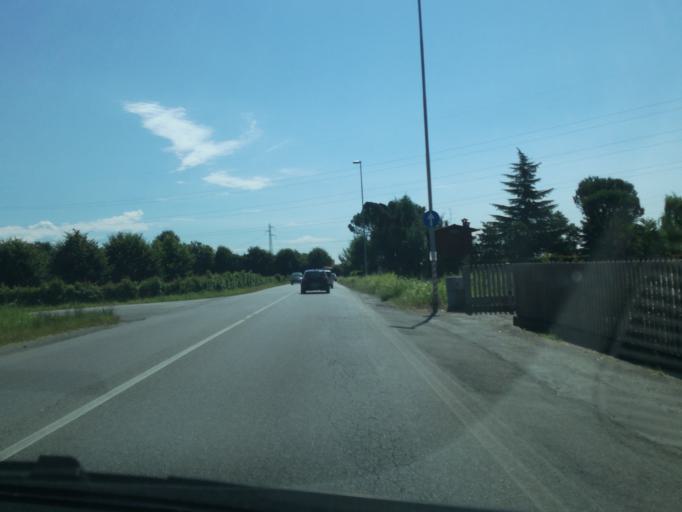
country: IT
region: Lombardy
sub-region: Provincia di Bergamo
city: Piazza Caduti
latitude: 45.6954
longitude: 9.5079
